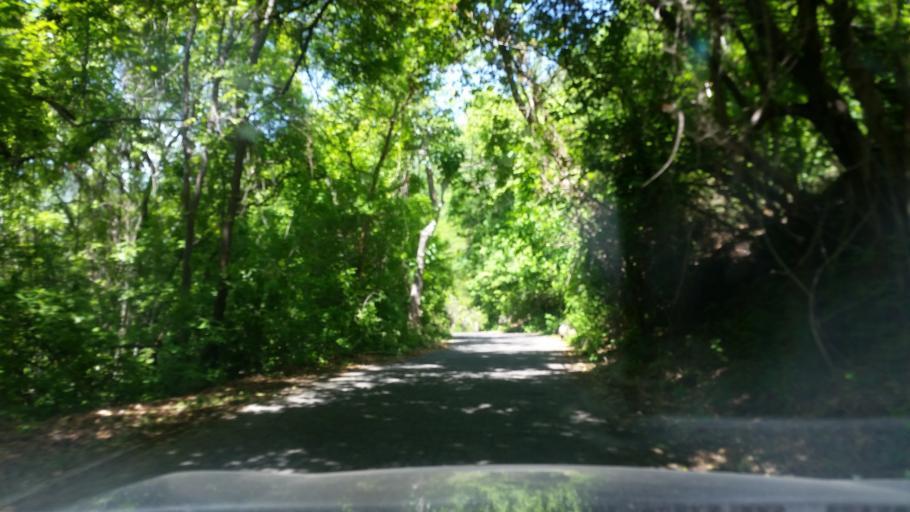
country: NI
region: Masaya
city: Catarina
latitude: 11.9260
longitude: -86.0560
